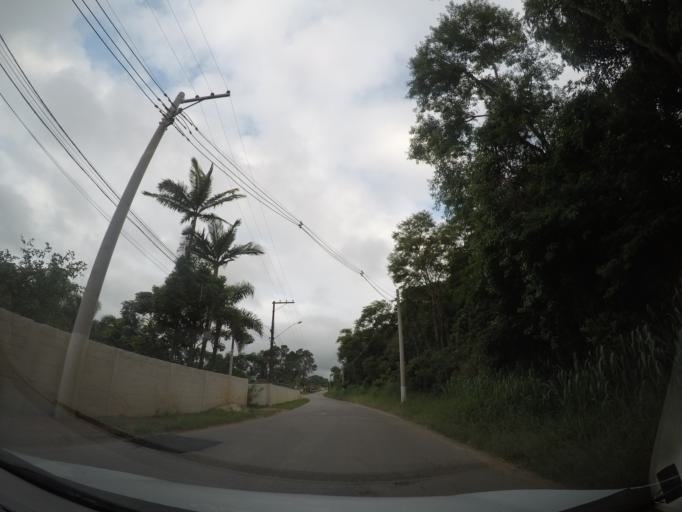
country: BR
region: Sao Paulo
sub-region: Aruja
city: Aruja
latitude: -23.3896
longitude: -46.3413
